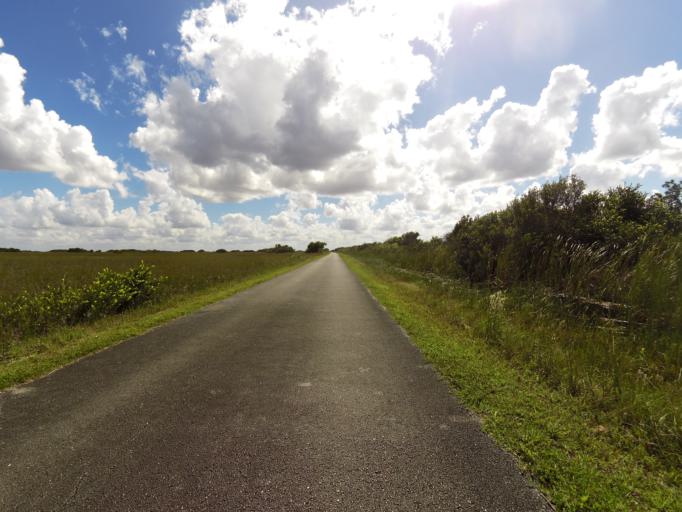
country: US
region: Florida
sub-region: Miami-Dade County
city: The Hammocks
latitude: 25.6936
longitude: -80.7669
